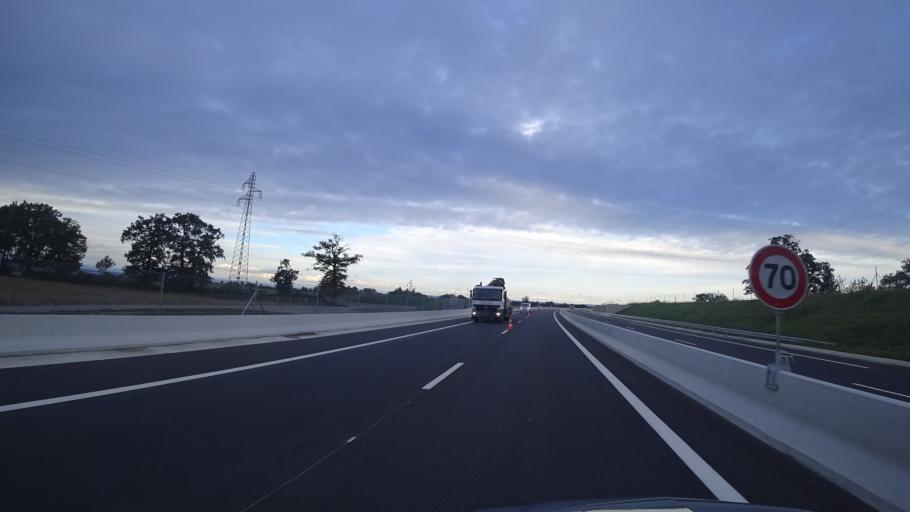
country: FR
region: Midi-Pyrenees
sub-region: Departement de l'Aveyron
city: Luc-la-Primaube
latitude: 44.2910
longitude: 2.4993
